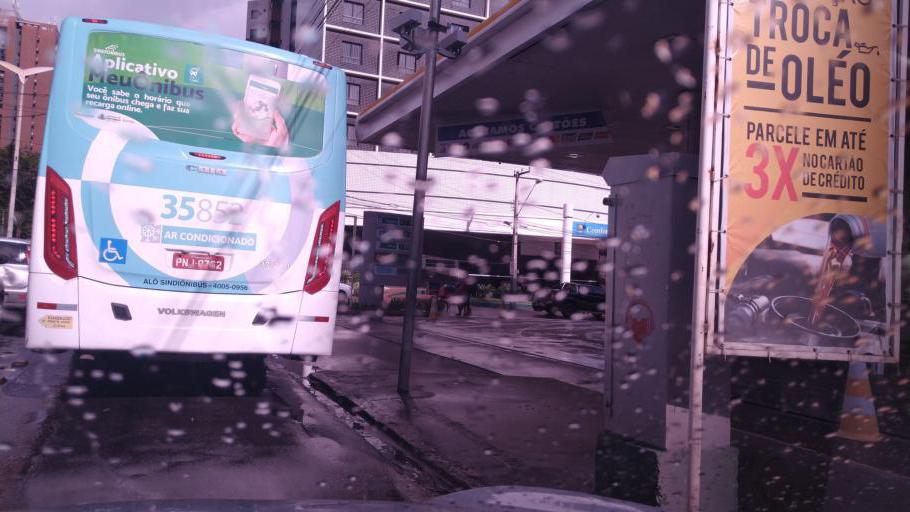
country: BR
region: Ceara
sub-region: Fortaleza
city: Fortaleza
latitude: -3.7262
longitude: -38.4891
